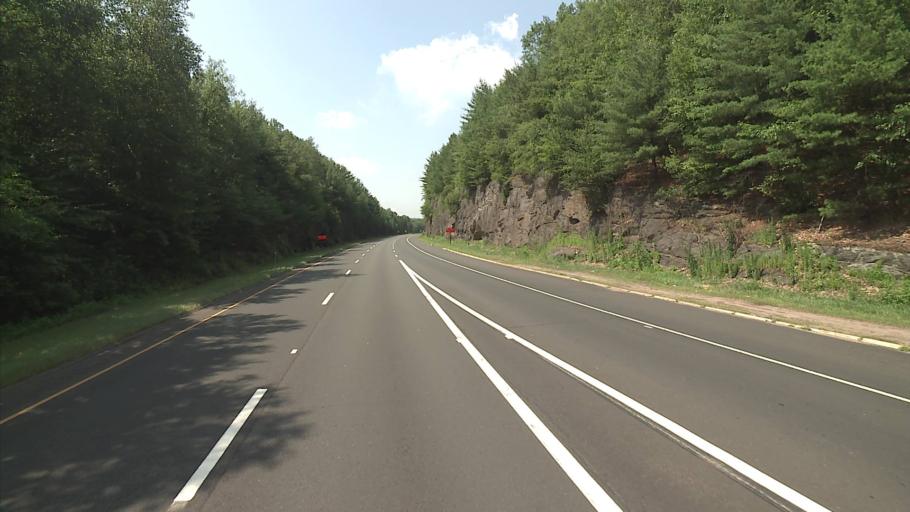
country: US
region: Connecticut
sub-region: Hartford County
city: Manchester
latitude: 41.7760
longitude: -72.4650
